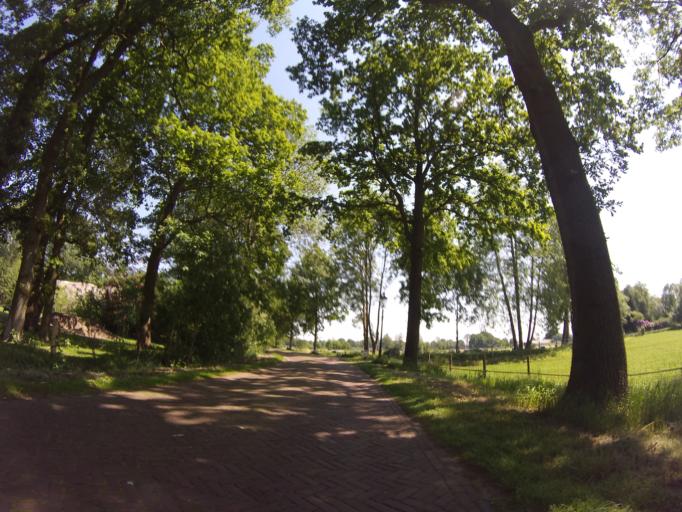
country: NL
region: Drenthe
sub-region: Gemeente Emmen
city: Schoonebeek
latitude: 52.6698
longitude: 6.8650
